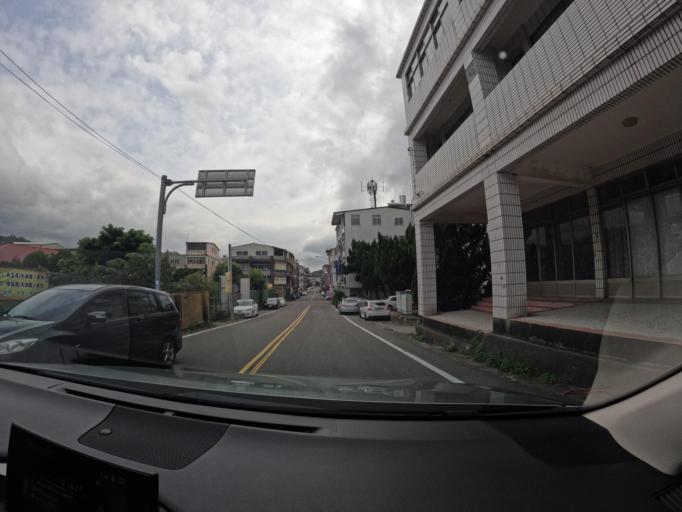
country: TW
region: Taiwan
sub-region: Miaoli
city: Miaoli
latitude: 24.4262
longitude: 120.8708
